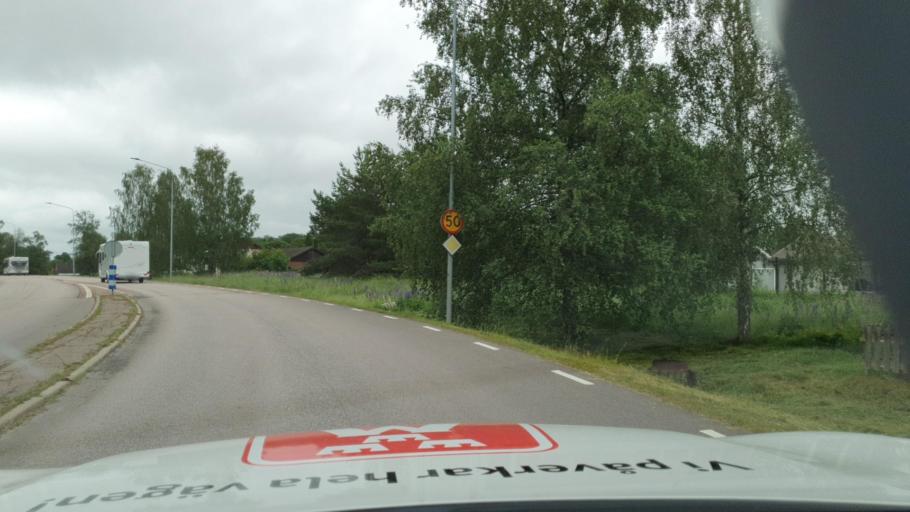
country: SE
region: Vaermland
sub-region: Karlstads Kommun
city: Valberg
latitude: 59.3847
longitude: 13.1774
